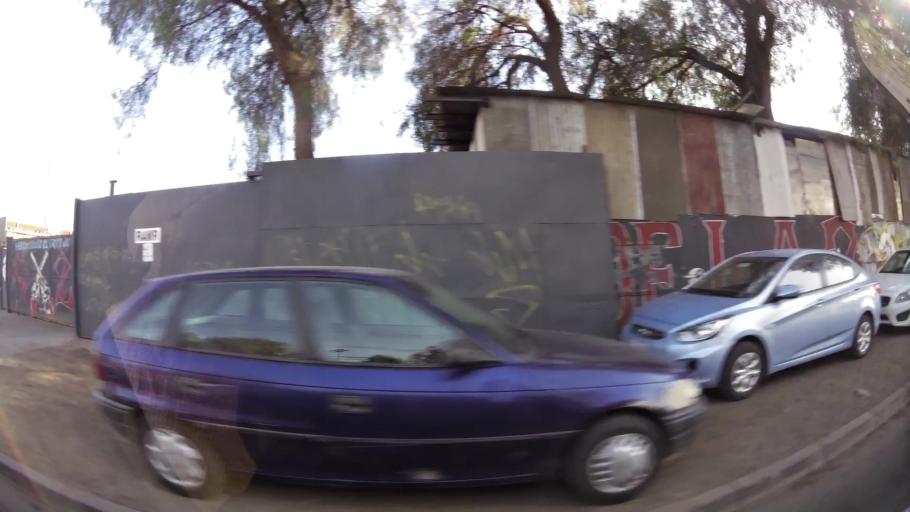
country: CL
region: Santiago Metropolitan
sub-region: Provincia de Santiago
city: Lo Prado
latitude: -33.4144
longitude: -70.7640
